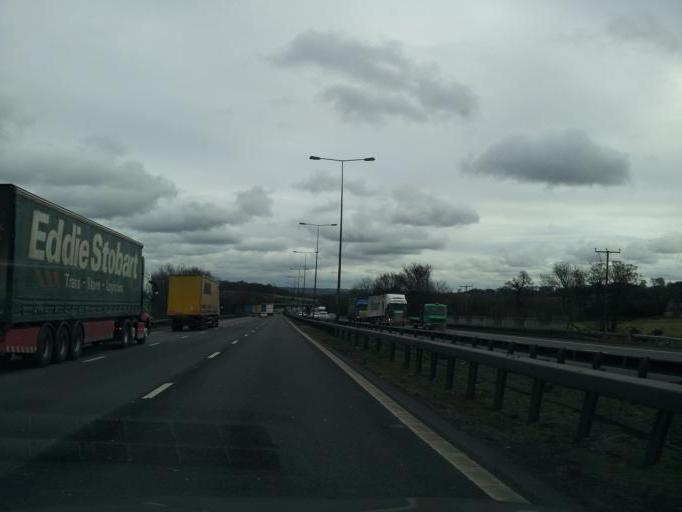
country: GB
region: England
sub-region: Staffordshire
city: Newcastle under Lyme
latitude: 52.9896
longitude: -2.2633
